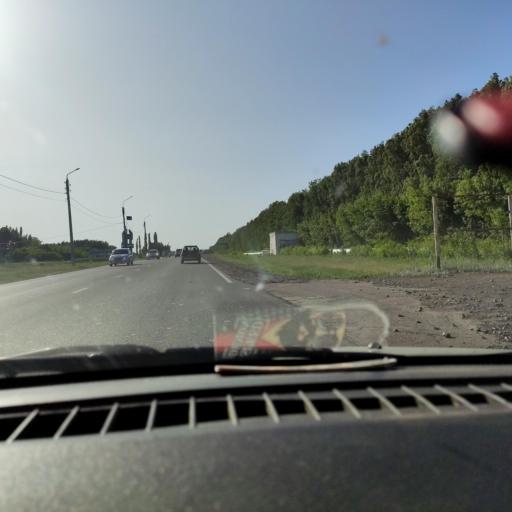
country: RU
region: Bashkortostan
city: Sterlitamak
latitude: 53.6455
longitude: 55.8872
